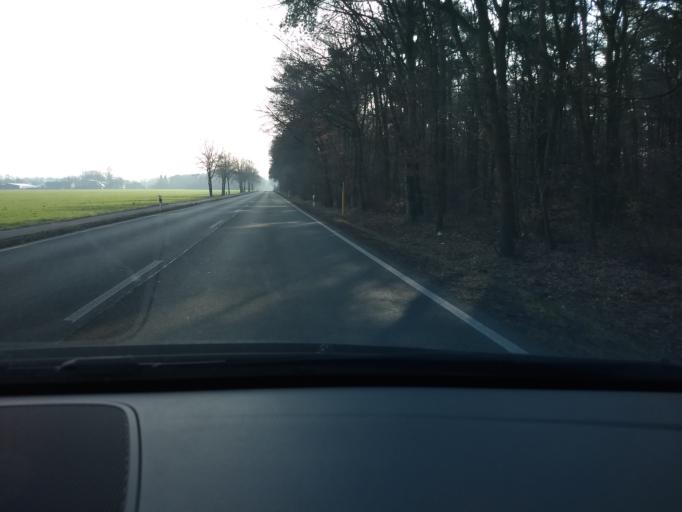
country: DE
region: North Rhine-Westphalia
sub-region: Regierungsbezirk Munster
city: Rhede
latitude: 51.8299
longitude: 6.7327
